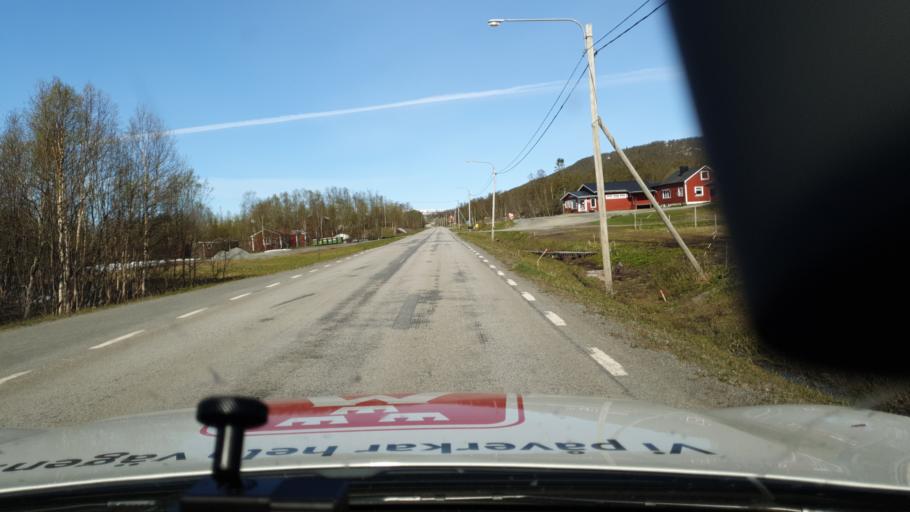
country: NO
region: Nordland
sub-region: Hattfjelldal
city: Hattfjelldal
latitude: 65.7425
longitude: 15.0213
